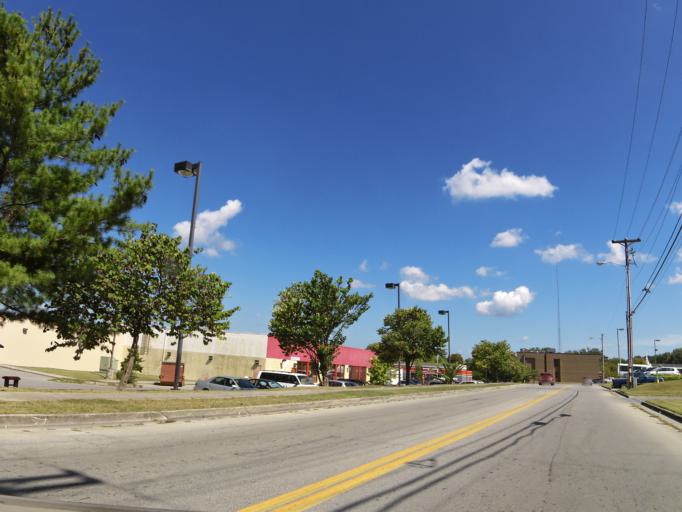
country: US
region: Tennessee
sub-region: Blount County
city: Maryville
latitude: 35.7628
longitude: -83.9712
